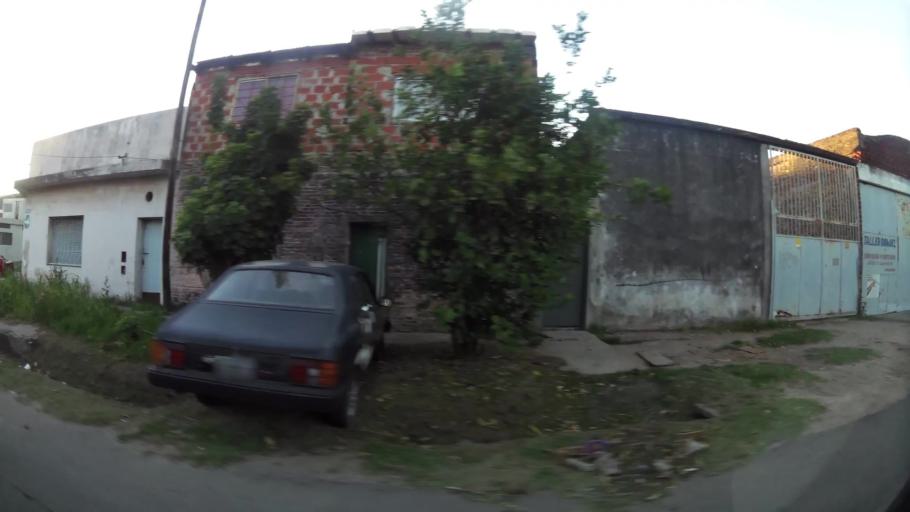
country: AR
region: Santa Fe
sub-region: Departamento de Rosario
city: Rosario
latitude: -32.9675
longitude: -60.6764
